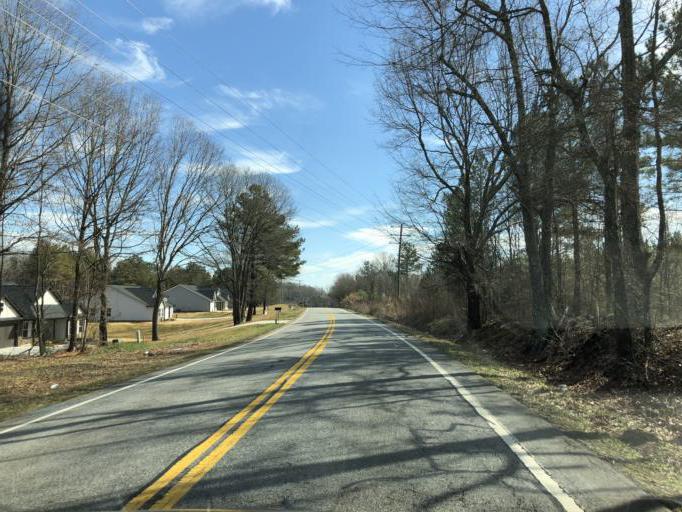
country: US
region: South Carolina
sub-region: Spartanburg County
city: Boiling Springs
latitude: 35.0541
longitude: -81.9347
